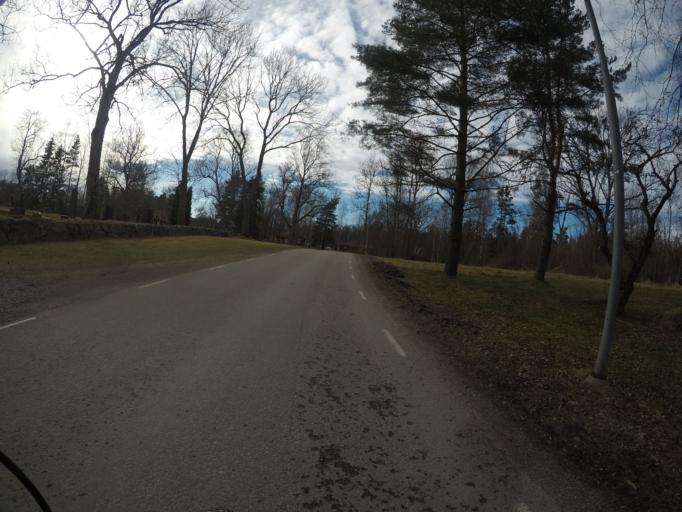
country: SE
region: Vaestmanland
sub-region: Kungsors Kommun
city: Kungsoer
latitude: 59.4223
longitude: 16.1870
